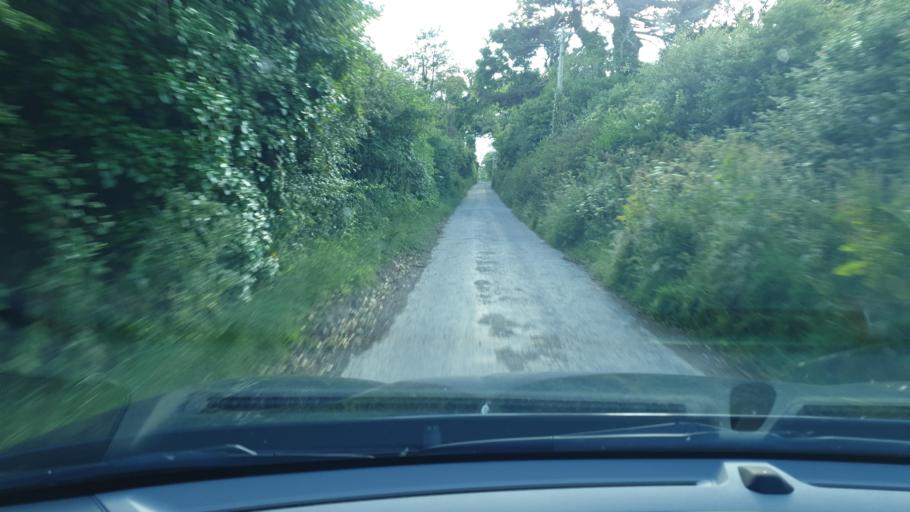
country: IE
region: Leinster
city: An Ros
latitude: 53.5510
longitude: -6.0899
